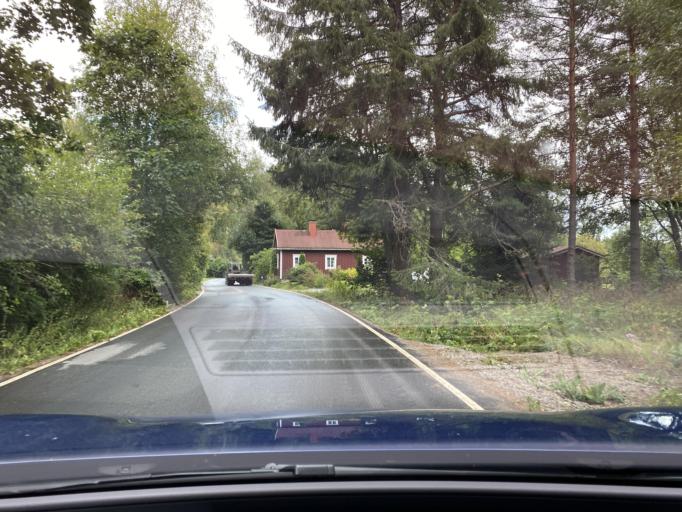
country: FI
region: Pirkanmaa
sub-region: Lounais-Pirkanmaa
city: Punkalaidun
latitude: 61.1676
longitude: 23.1801
